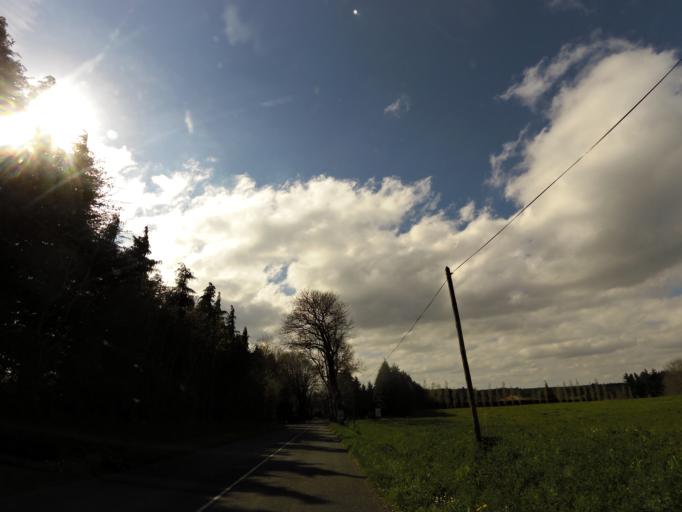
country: FR
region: Midi-Pyrenees
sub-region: Departement du Tarn
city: Soreze
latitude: 43.4061
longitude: 2.0843
